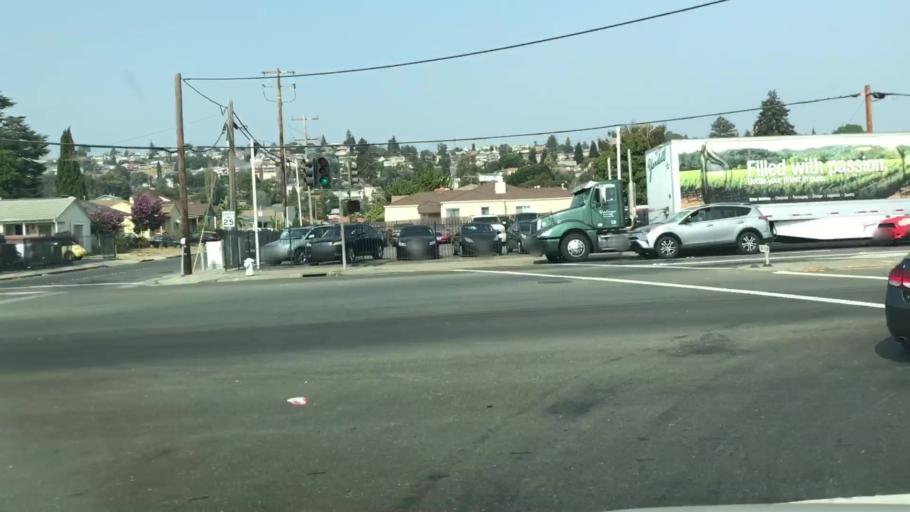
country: US
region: California
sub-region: Alameda County
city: Ashland
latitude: 37.6902
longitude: -122.1075
